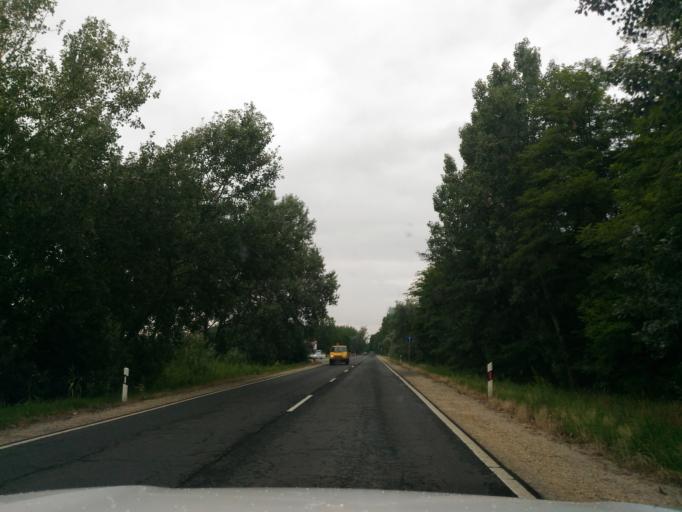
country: HU
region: Pest
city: Ocsa
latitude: 47.2877
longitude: 19.1920
